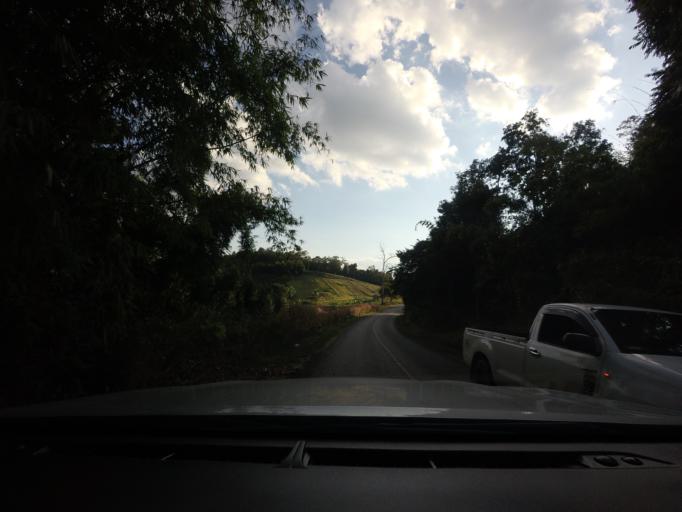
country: TH
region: Chiang Mai
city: Phrao
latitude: 19.5316
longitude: 99.1599
